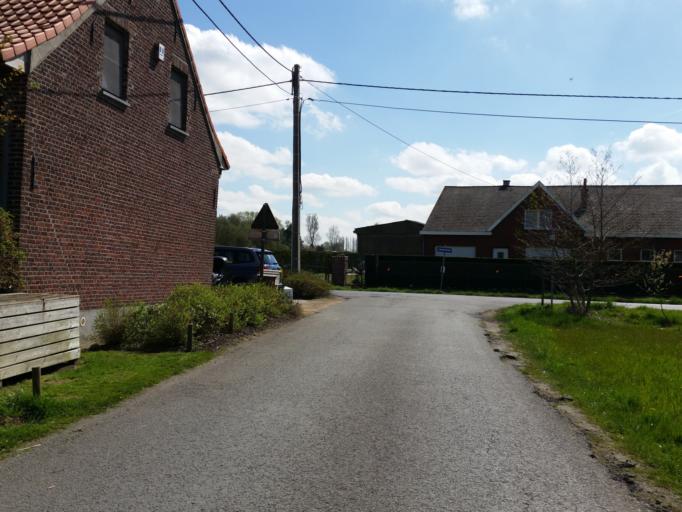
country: BE
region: Flanders
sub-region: Provincie Vlaams-Brabant
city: Boortmeerbeek
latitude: 50.9746
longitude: 4.5533
